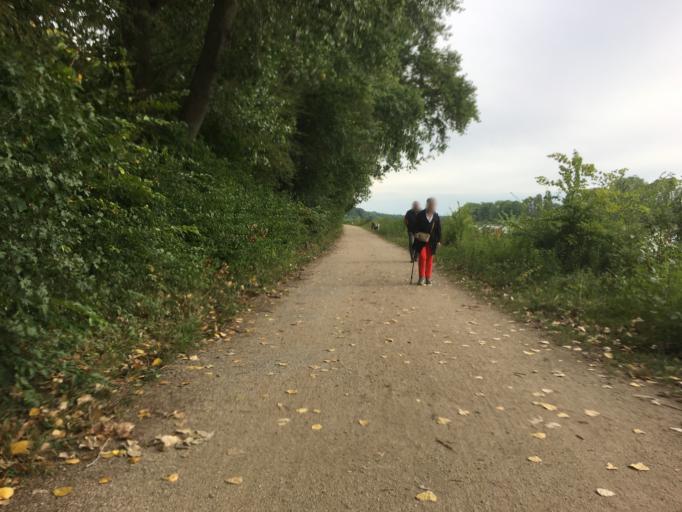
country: DE
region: Baden-Wuerttemberg
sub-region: Karlsruhe Region
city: Bruhl
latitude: 49.3997
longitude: 8.4986
